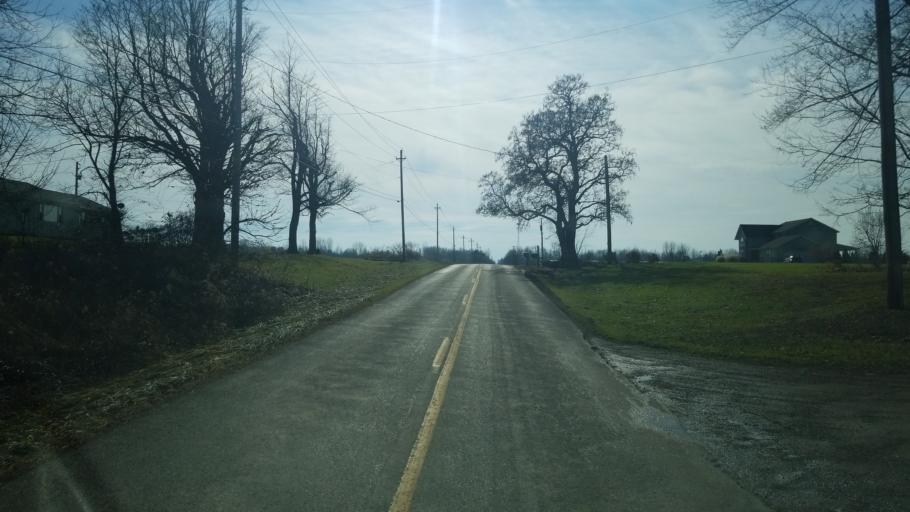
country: US
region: Ohio
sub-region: Ashtabula County
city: Roaming Shores
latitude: 41.6902
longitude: -80.8359
